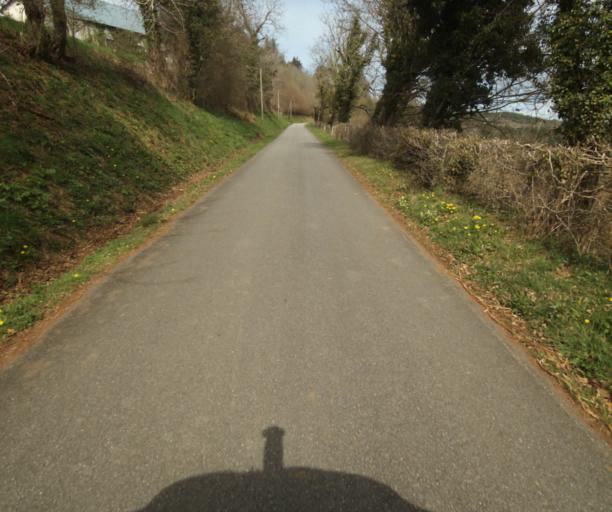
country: FR
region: Limousin
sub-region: Departement de la Correze
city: Naves
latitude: 45.3236
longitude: 1.8071
